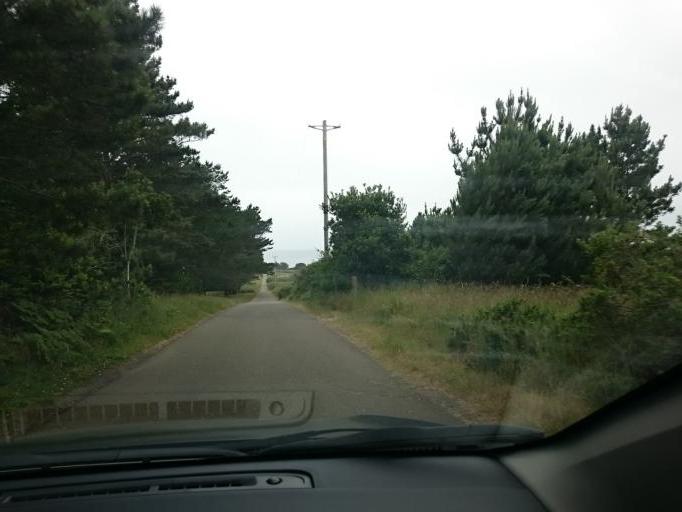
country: US
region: California
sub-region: Mendocino County
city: Fort Bragg
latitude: 39.3494
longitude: -123.8148
